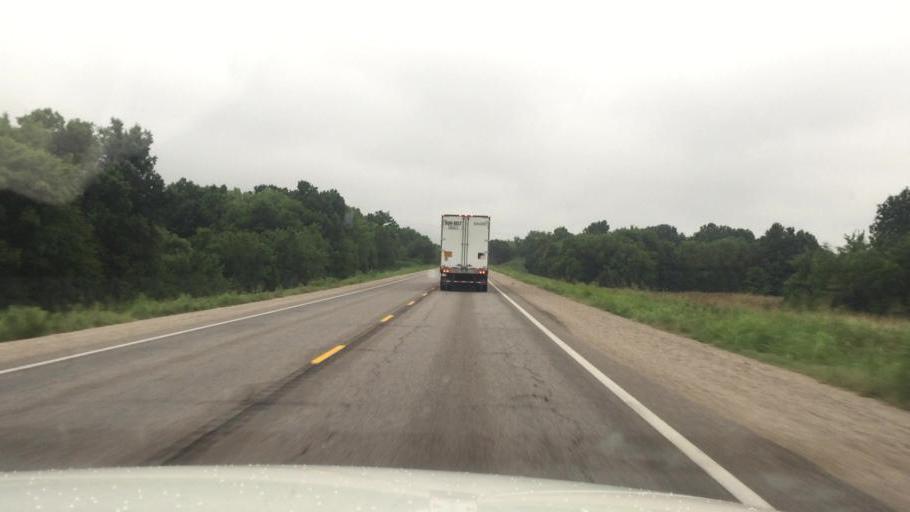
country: US
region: Kansas
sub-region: Montgomery County
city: Cherryvale
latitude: 37.1646
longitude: -95.5767
